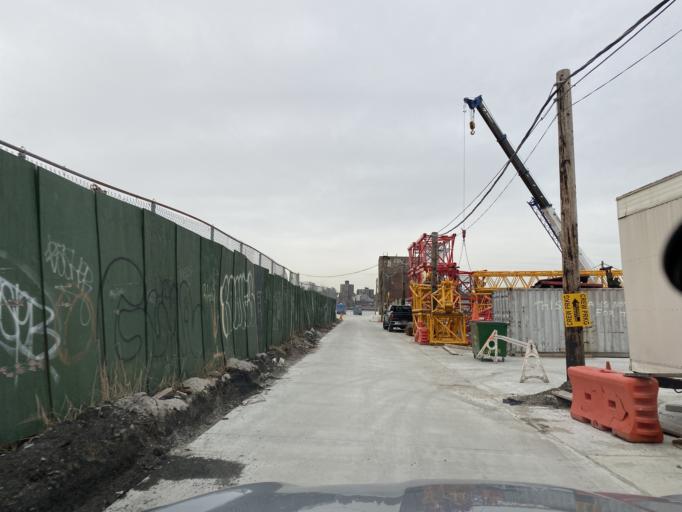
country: US
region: New York
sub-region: Queens County
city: Long Island City
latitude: 40.7276
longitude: -73.9593
